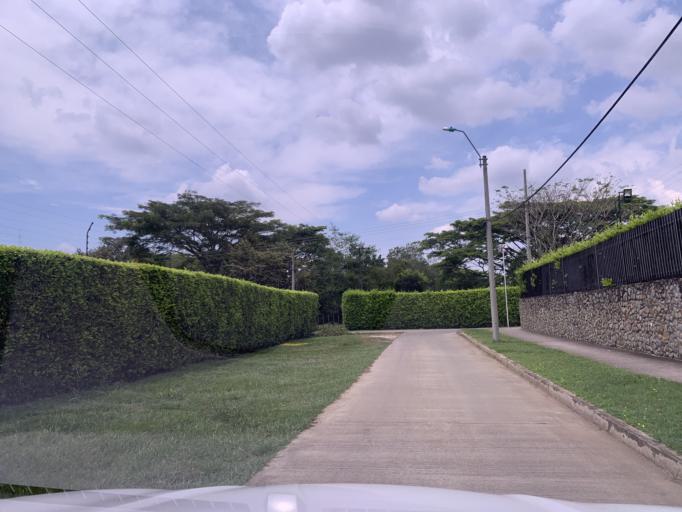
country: CO
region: Valle del Cauca
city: Jamundi
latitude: 3.3085
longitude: -76.5350
